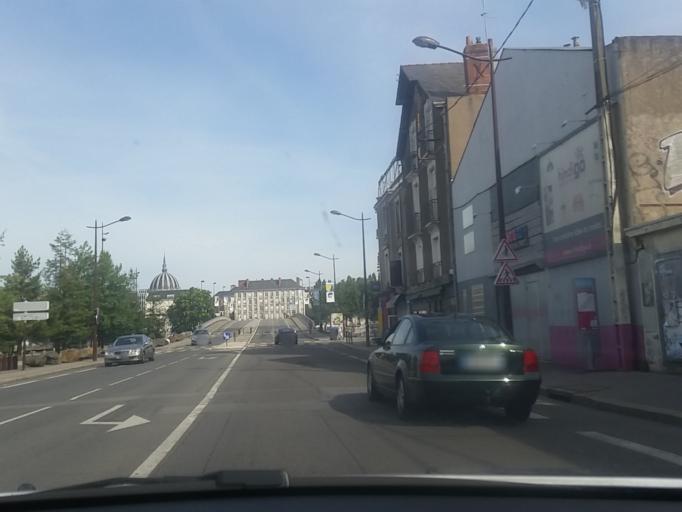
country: FR
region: Pays de la Loire
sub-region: Departement de la Loire-Atlantique
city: Nantes
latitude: 47.2069
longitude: -1.5645
